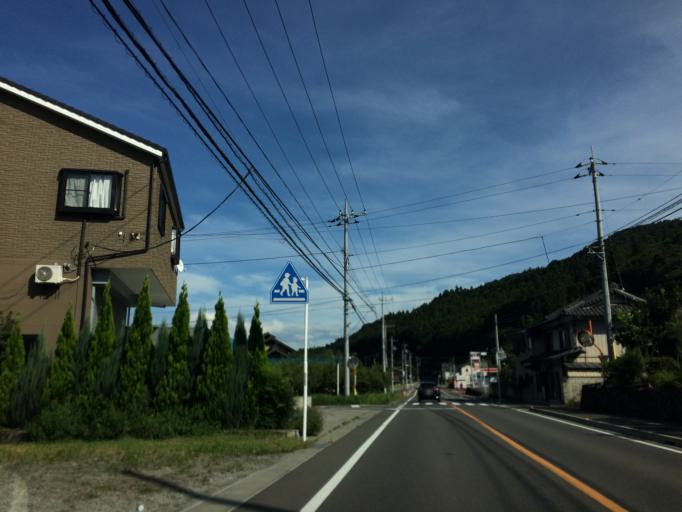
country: JP
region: Gunma
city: Nakanojomachi
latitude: 36.5515
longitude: 138.9061
